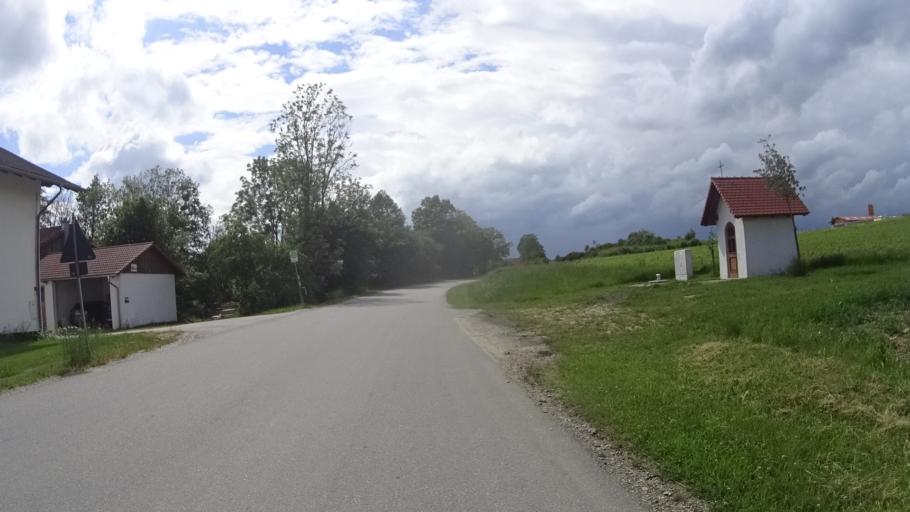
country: DE
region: Bavaria
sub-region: Lower Bavaria
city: Gangkofen
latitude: 48.4479
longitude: 12.5181
